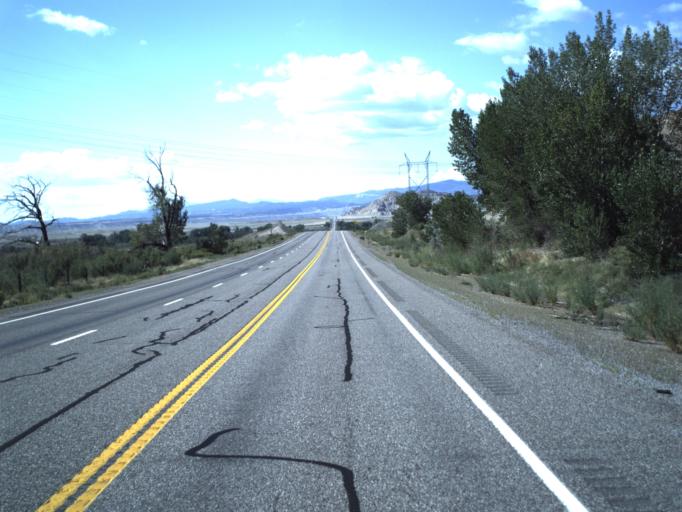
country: US
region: Utah
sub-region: Emery County
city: Ferron
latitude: 38.8854
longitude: -111.2849
